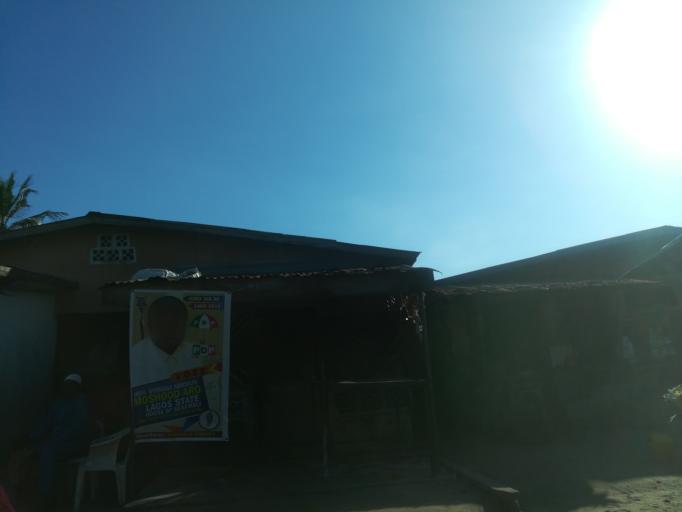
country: NG
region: Lagos
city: Ikorodu
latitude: 6.5376
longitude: 3.5525
